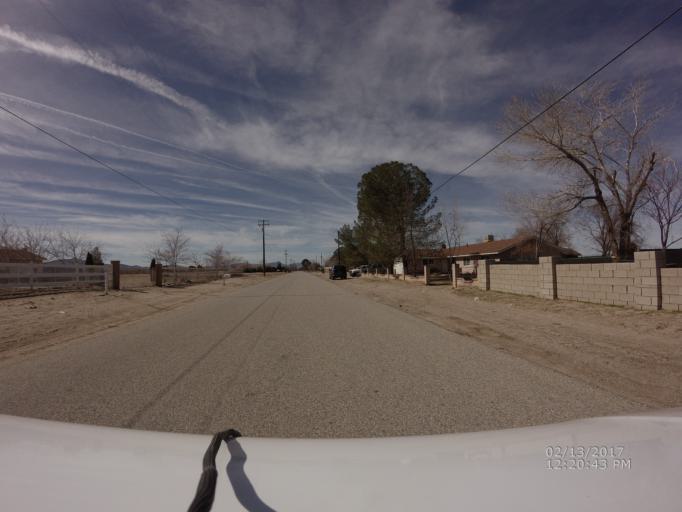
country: US
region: California
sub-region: Los Angeles County
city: Littlerock
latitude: 34.5653
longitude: -117.9279
